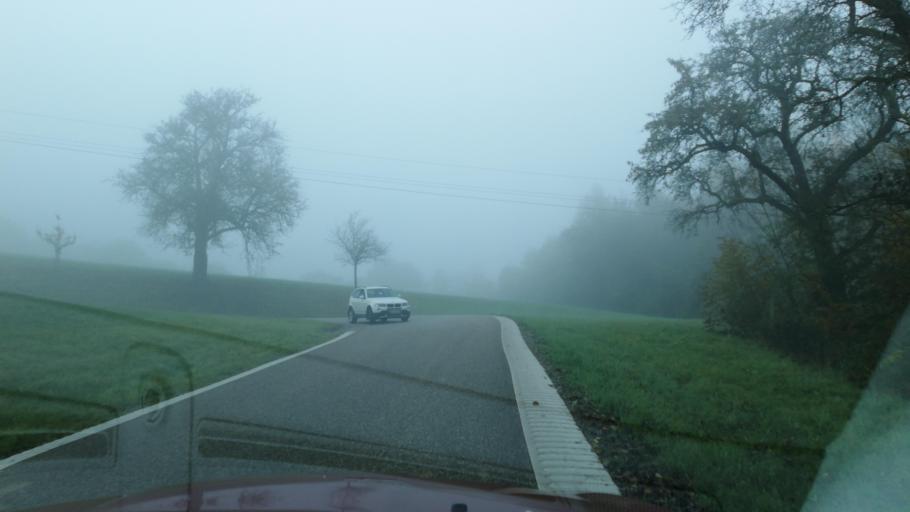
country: AT
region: Upper Austria
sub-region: Politischer Bezirk Grieskirchen
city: Bad Schallerbach
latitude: 48.2139
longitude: 13.8854
